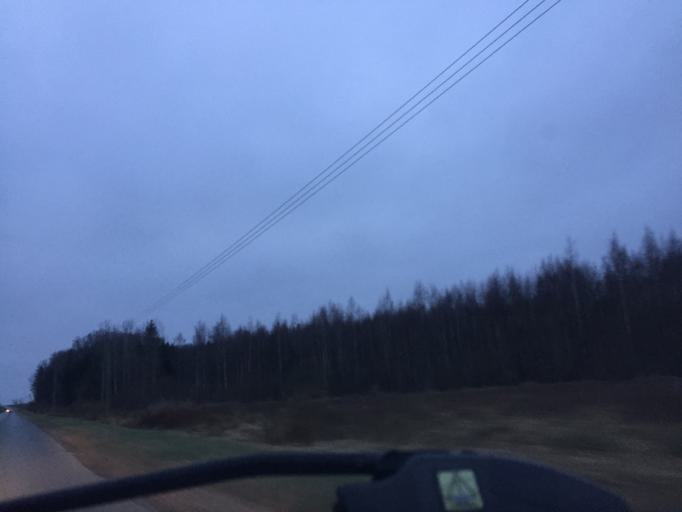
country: LV
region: Limbazu Rajons
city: Limbazi
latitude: 57.5960
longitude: 24.7948
